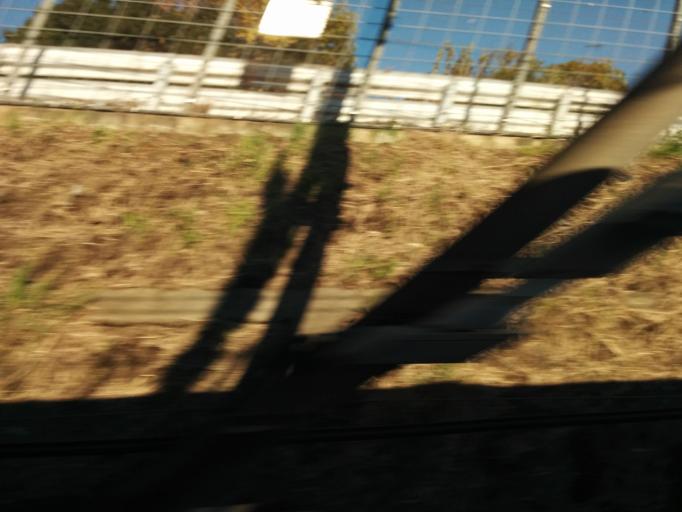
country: JP
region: Kanagawa
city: Minami-rinkan
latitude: 35.4268
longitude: 139.4530
